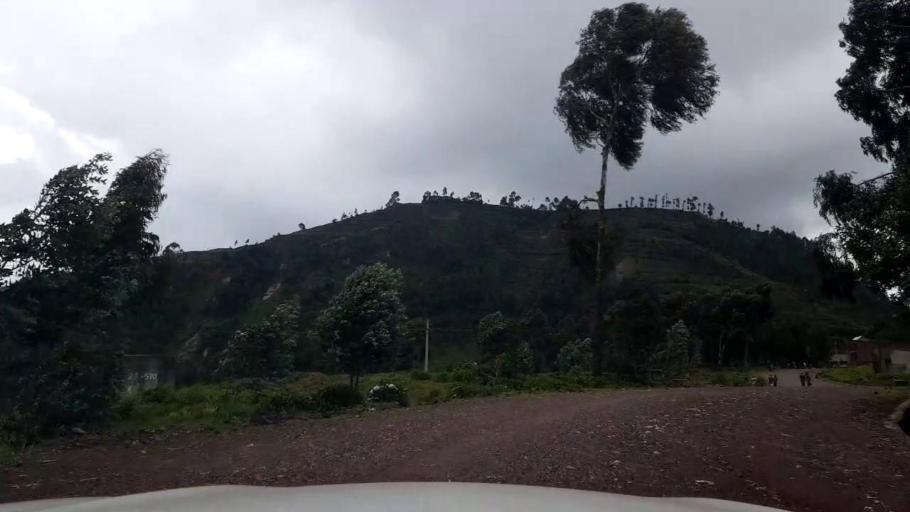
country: RW
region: Northern Province
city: Musanze
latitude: -1.5893
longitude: 29.4686
